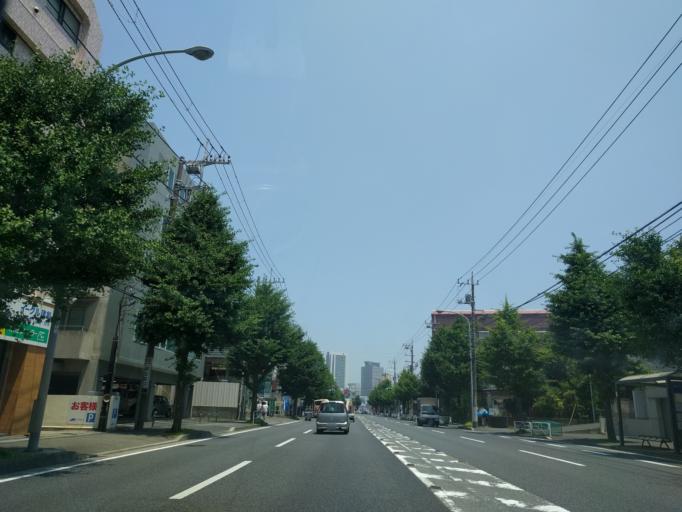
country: JP
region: Kanagawa
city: Yokohama
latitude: 35.3983
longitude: 139.5876
